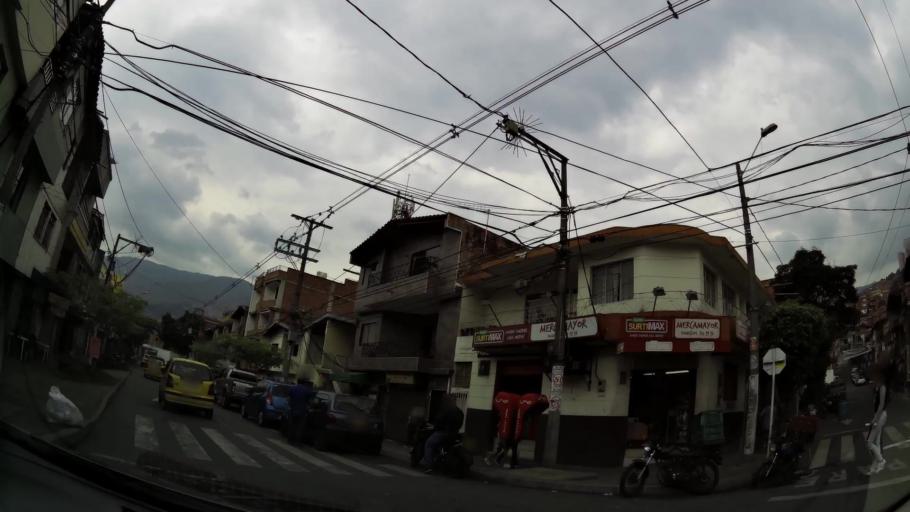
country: CO
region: Antioquia
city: Medellin
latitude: 6.2368
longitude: -75.5618
